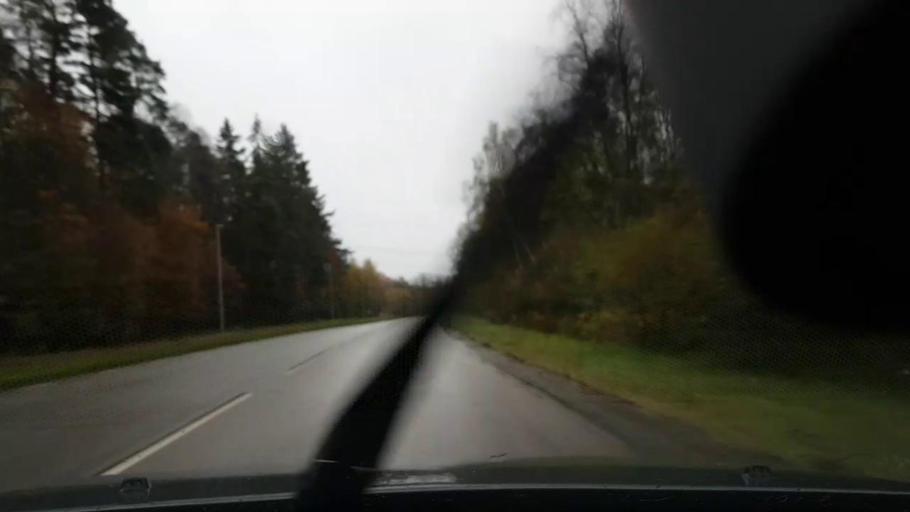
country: SE
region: Vaestra Goetaland
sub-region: Molndal
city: Kallered
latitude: 57.5998
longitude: 12.0822
